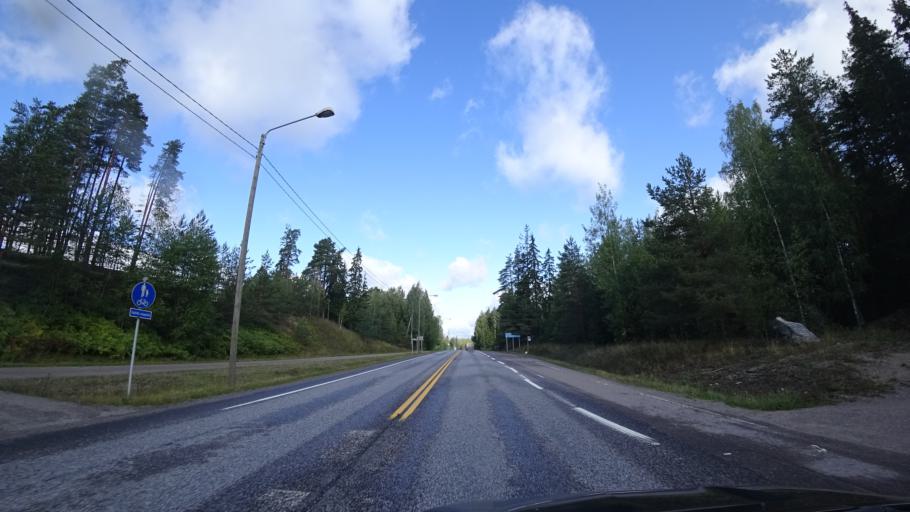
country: FI
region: Uusimaa
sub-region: Helsinki
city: Tuusula
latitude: 60.4395
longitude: 24.9792
